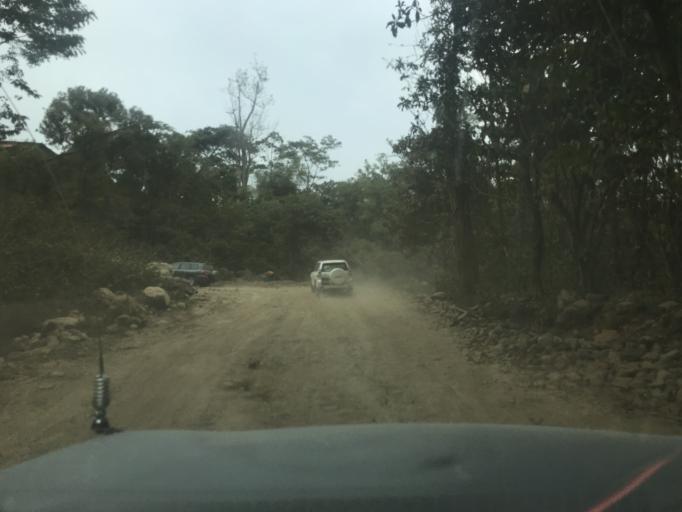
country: TL
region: Ainaro
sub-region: Ainaro
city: Ainaro
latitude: -8.9906
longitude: 125.5113
